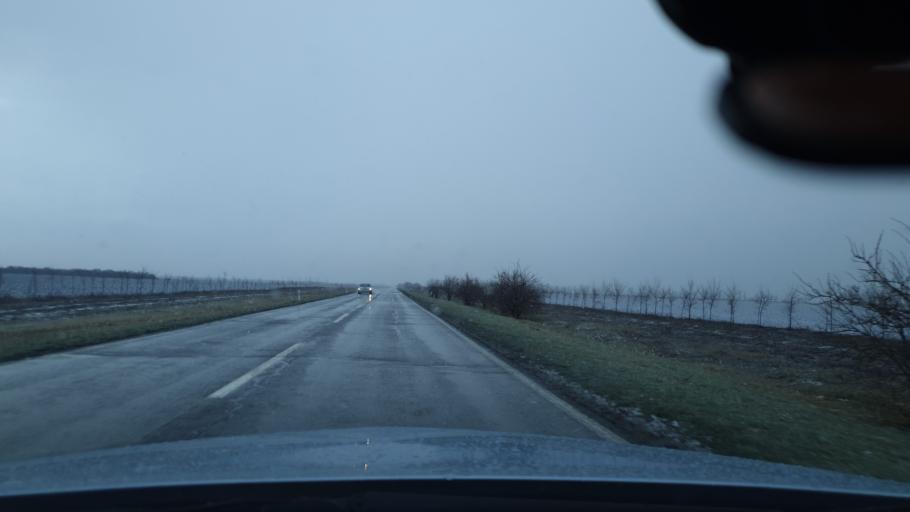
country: RS
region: Autonomna Pokrajina Vojvodina
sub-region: Juznobanatski Okrug
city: Pancevo
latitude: 44.8569
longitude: 20.7533
